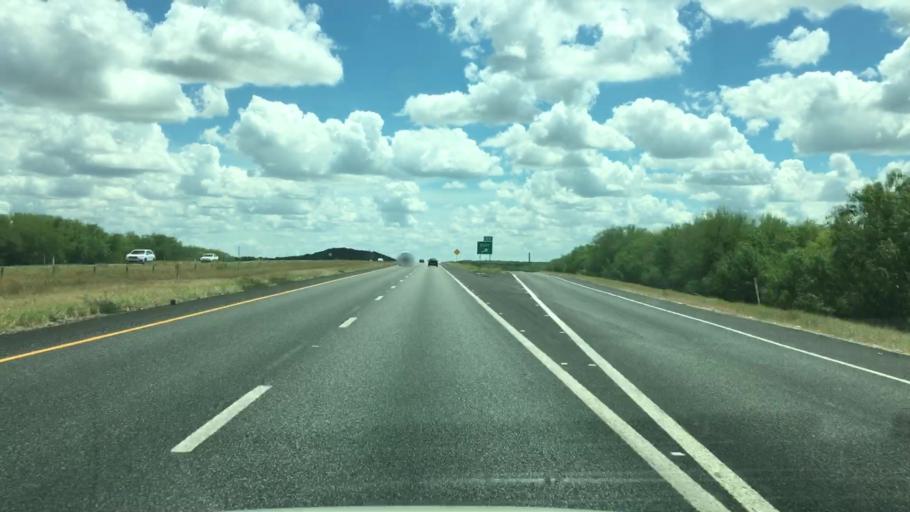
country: US
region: Texas
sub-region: Atascosa County
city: Pleasanton
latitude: 28.7378
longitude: -98.2908
